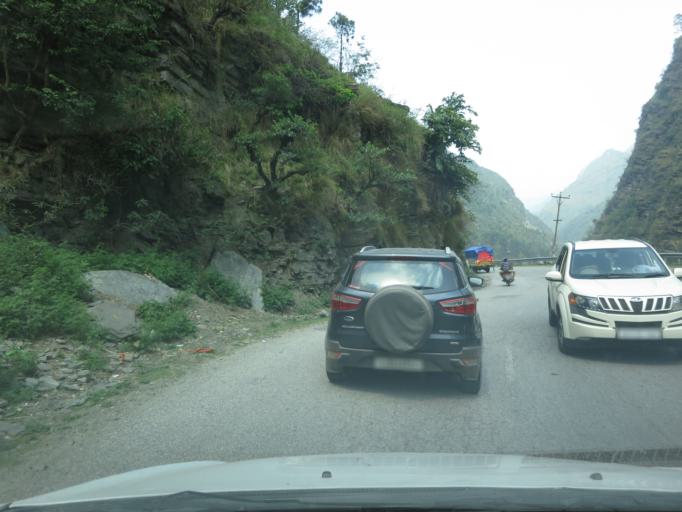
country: IN
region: Himachal Pradesh
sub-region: Mandi
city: Pandoh
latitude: 31.6935
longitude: 77.1359
